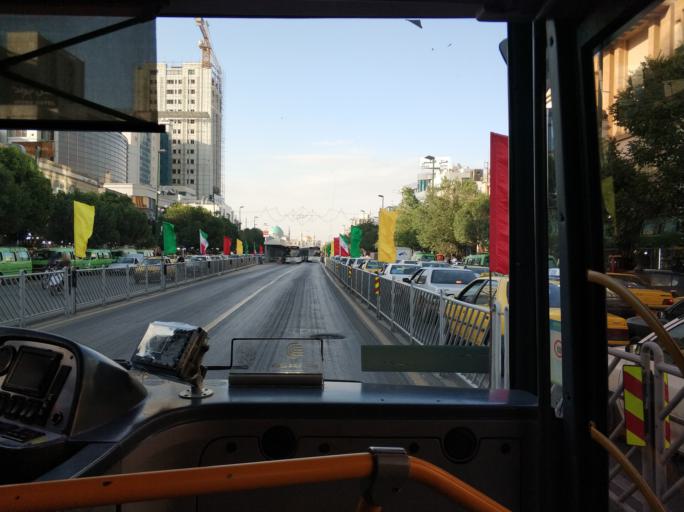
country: IR
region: Razavi Khorasan
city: Mashhad
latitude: 36.2817
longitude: 59.6104
